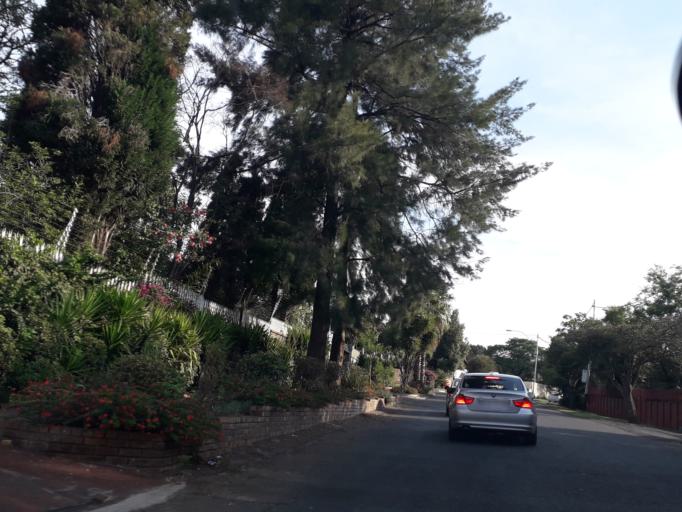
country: ZA
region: Gauteng
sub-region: City of Johannesburg Metropolitan Municipality
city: Johannesburg
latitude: -26.1215
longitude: 27.9990
